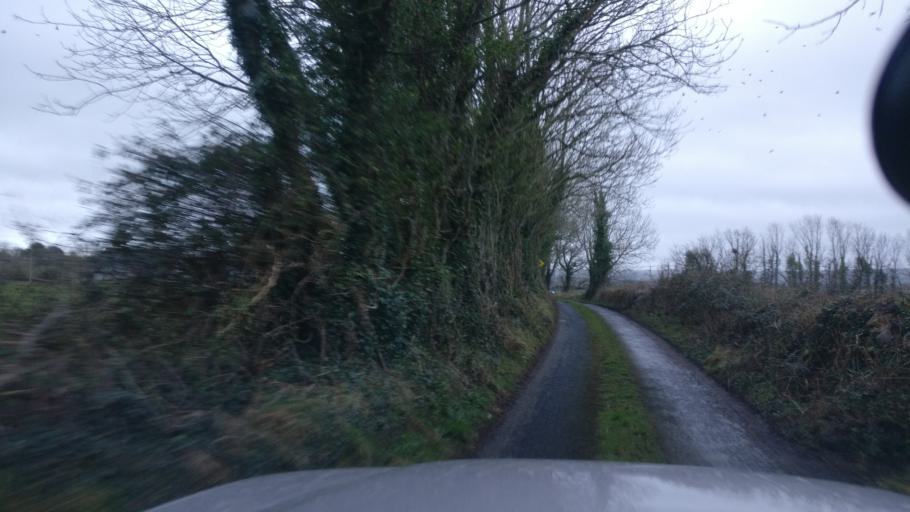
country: IE
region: Connaught
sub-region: County Galway
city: Loughrea
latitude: 53.1984
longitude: -8.6412
